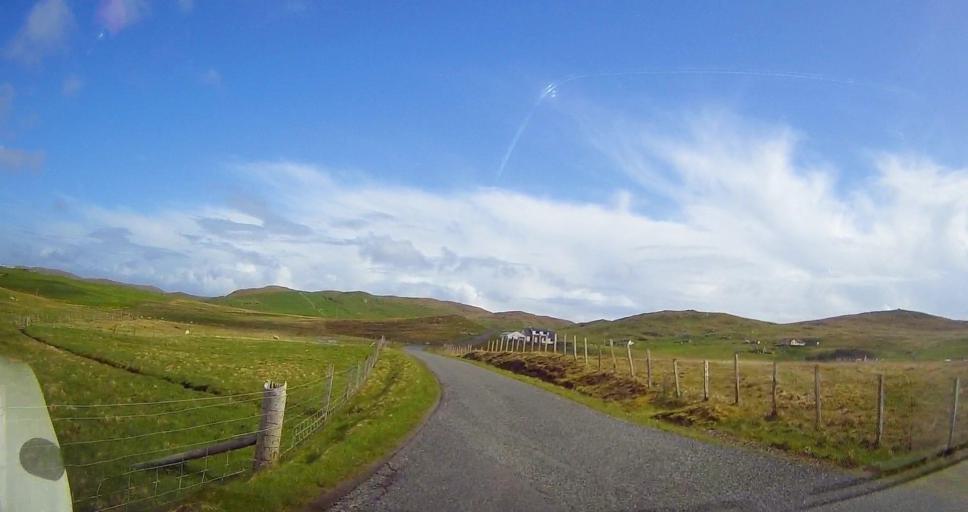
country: GB
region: Scotland
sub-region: Shetland Islands
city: Lerwick
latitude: 60.5904
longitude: -1.3348
